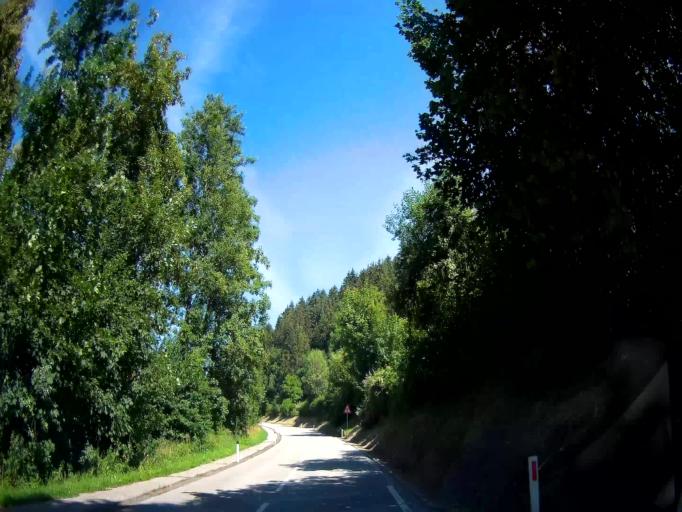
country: AT
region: Carinthia
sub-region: Politischer Bezirk Sankt Veit an der Glan
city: St. Georgen am Laengsee
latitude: 46.7635
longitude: 14.4240
